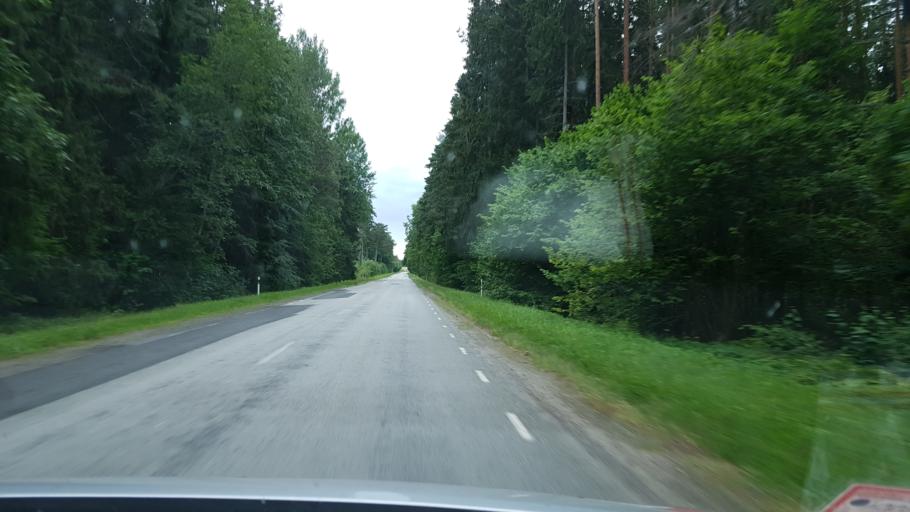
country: EE
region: Polvamaa
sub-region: Raepina vald
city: Rapina
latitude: 58.0815
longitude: 27.4320
